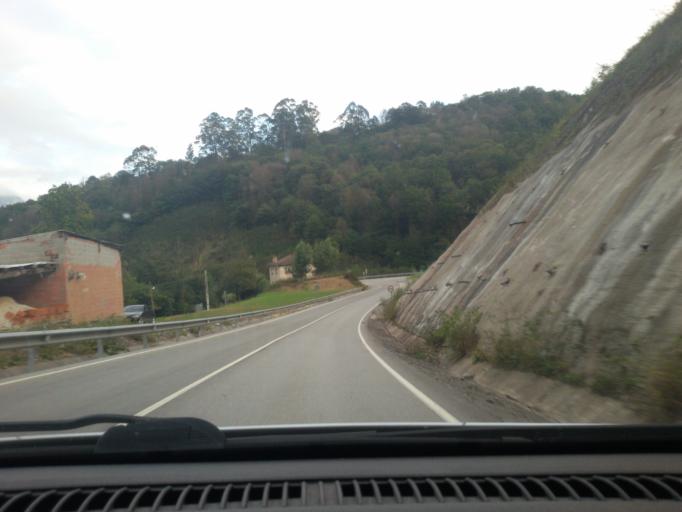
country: ES
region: Asturias
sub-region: Province of Asturias
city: Bimenes
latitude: 43.3394
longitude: -5.5778
